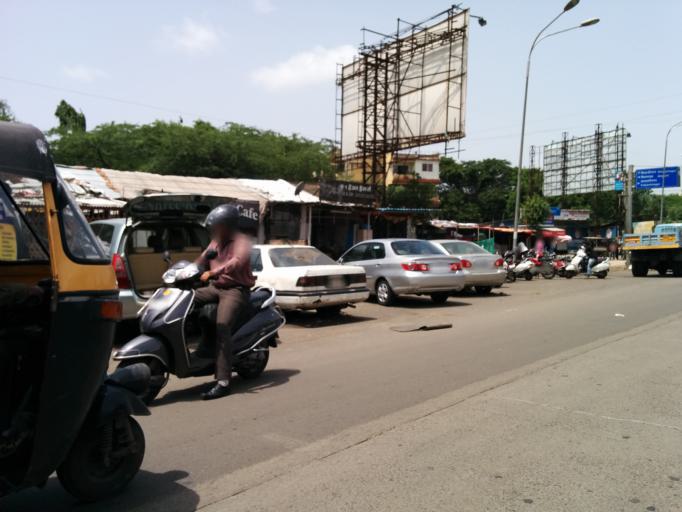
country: IN
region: Maharashtra
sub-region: Pune Division
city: Lohogaon
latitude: 18.5576
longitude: 73.9096
